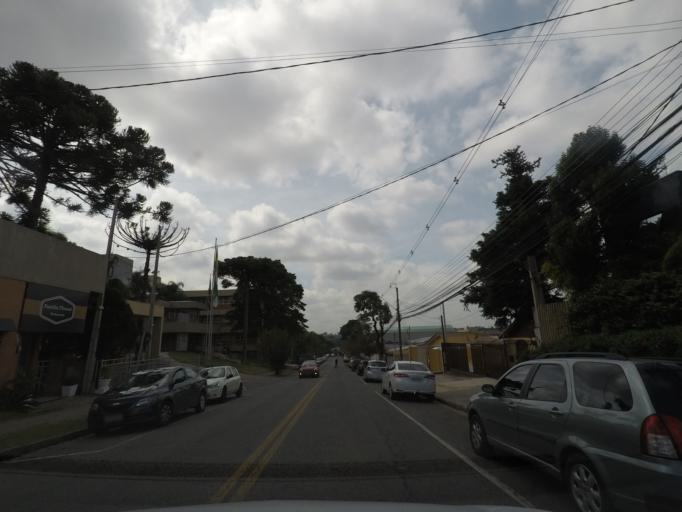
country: BR
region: Parana
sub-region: Curitiba
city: Curitiba
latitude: -25.4571
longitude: -49.2580
